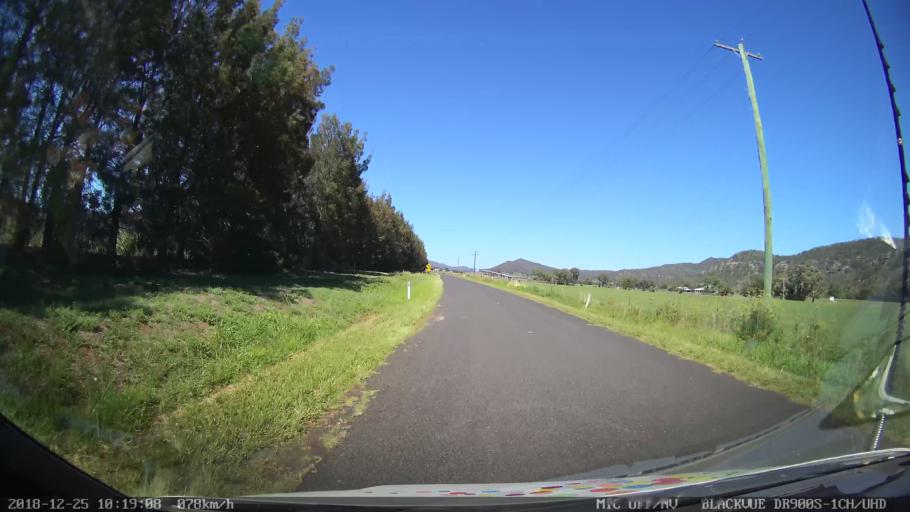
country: AU
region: New South Wales
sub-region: Muswellbrook
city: Denman
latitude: -32.3482
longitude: 150.5613
